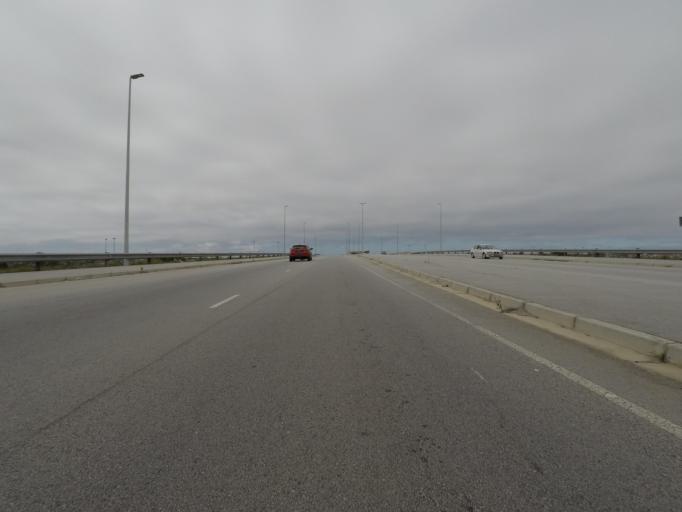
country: ZA
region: Eastern Cape
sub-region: Nelson Mandela Bay Metropolitan Municipality
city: Port Elizabeth
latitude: -33.9482
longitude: 25.4647
